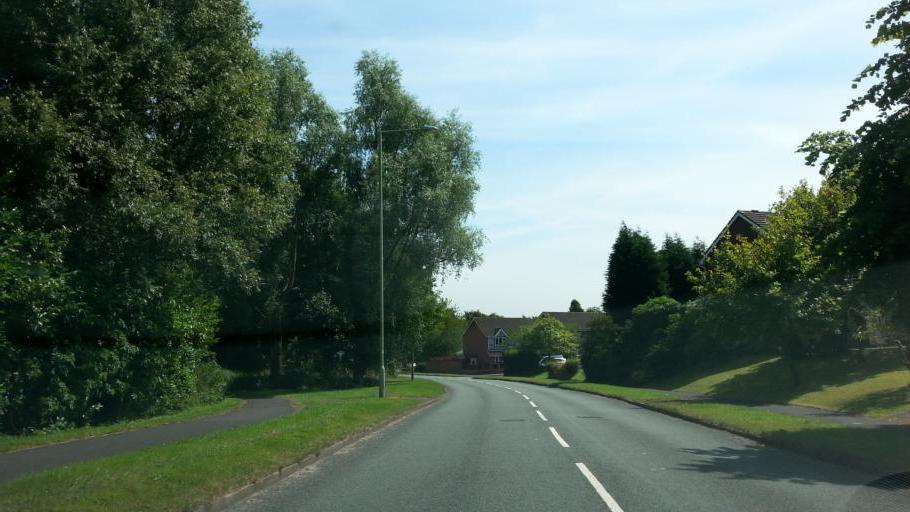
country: GB
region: England
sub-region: Staffordshire
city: Cannock
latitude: 52.7211
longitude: -2.0181
